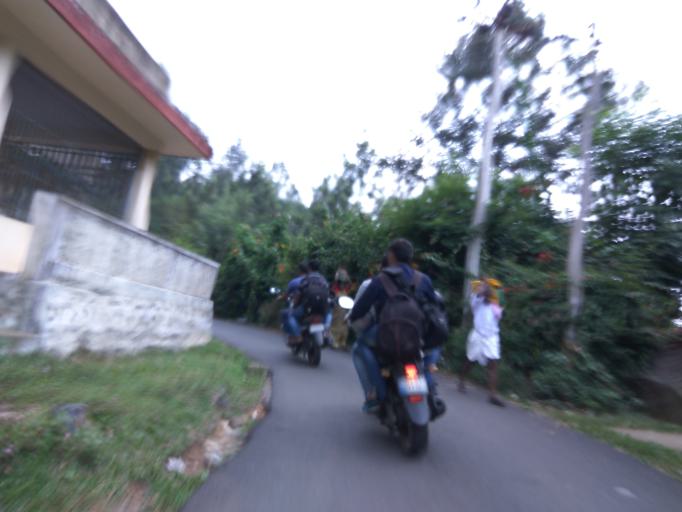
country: IN
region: Tamil Nadu
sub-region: Salem
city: Salem
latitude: 11.7880
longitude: 78.2069
